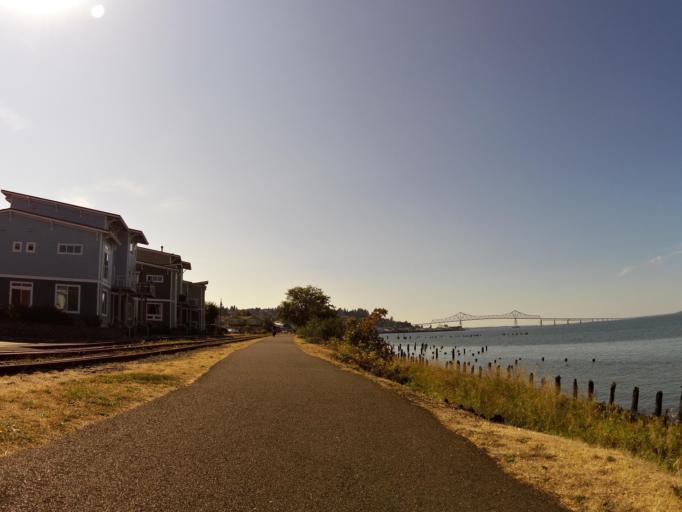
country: US
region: Oregon
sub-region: Clatsop County
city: Astoria
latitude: 46.1920
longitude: -123.8123
